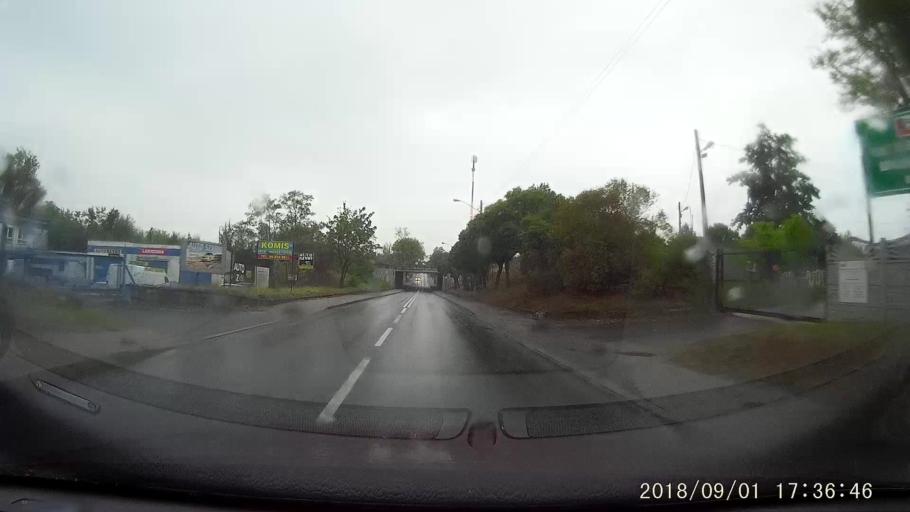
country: PL
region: Lubusz
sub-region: Powiat zaganski
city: Zagan
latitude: 51.6124
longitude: 15.3044
